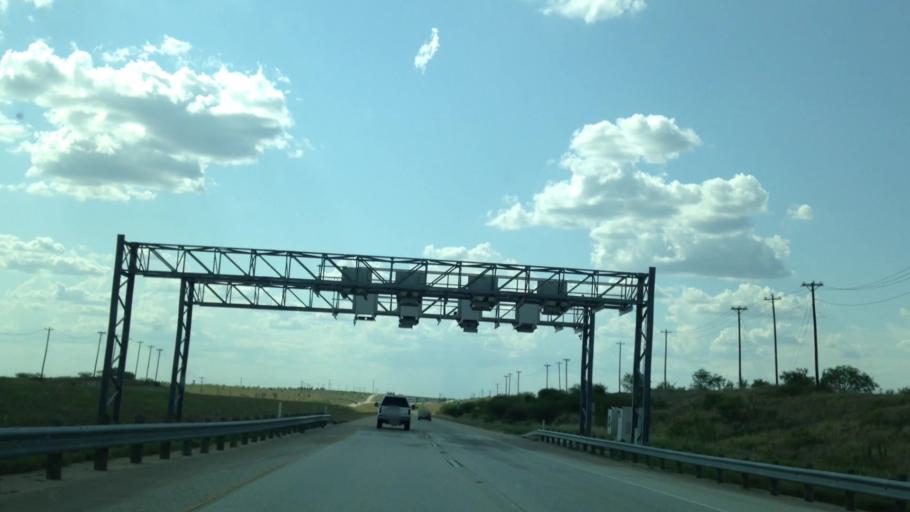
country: US
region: Texas
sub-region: Travis County
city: Onion Creek
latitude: 30.0951
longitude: -97.7629
